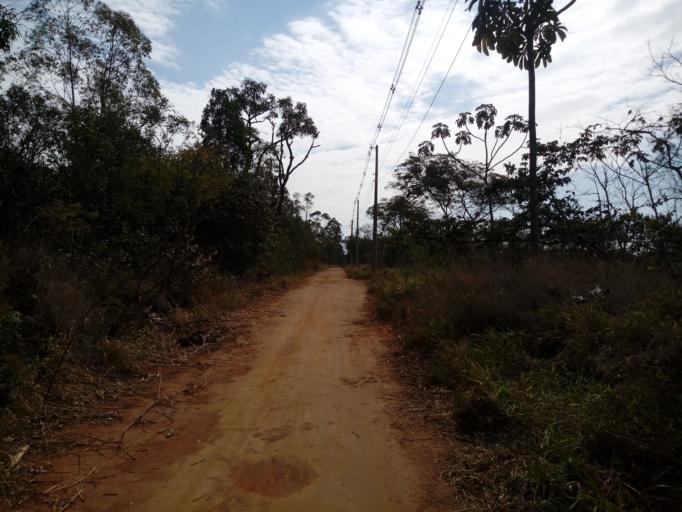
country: BR
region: Sao Paulo
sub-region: Sao Carlos
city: Sao Carlos
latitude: -21.9756
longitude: -47.8750
